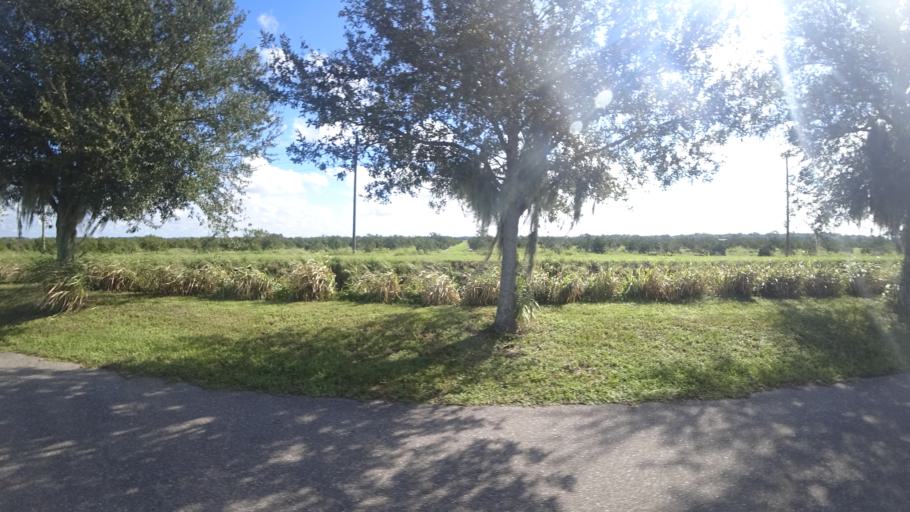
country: US
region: Florida
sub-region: Manatee County
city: Ellenton
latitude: 27.5812
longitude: -82.4747
